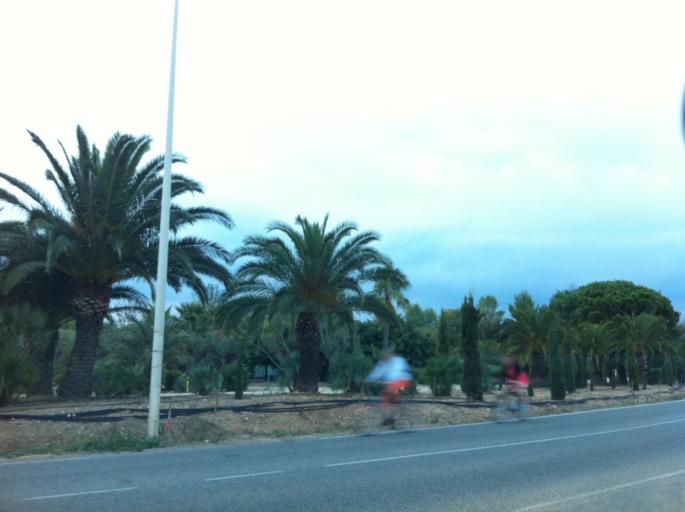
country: FR
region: Provence-Alpes-Cote d'Azur
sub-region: Departement du Var
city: Gassin
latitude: 43.2556
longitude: 6.5944
